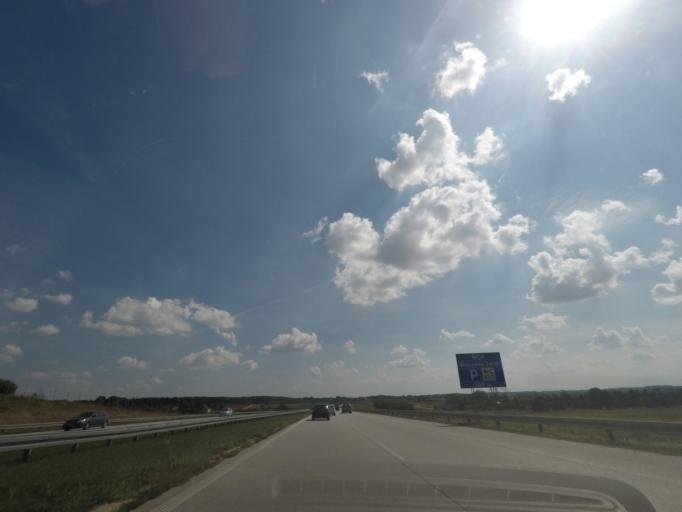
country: PL
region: Lodz Voivodeship
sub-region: Powiat zgierski
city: Strykow
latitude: 51.8509
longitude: 19.6600
